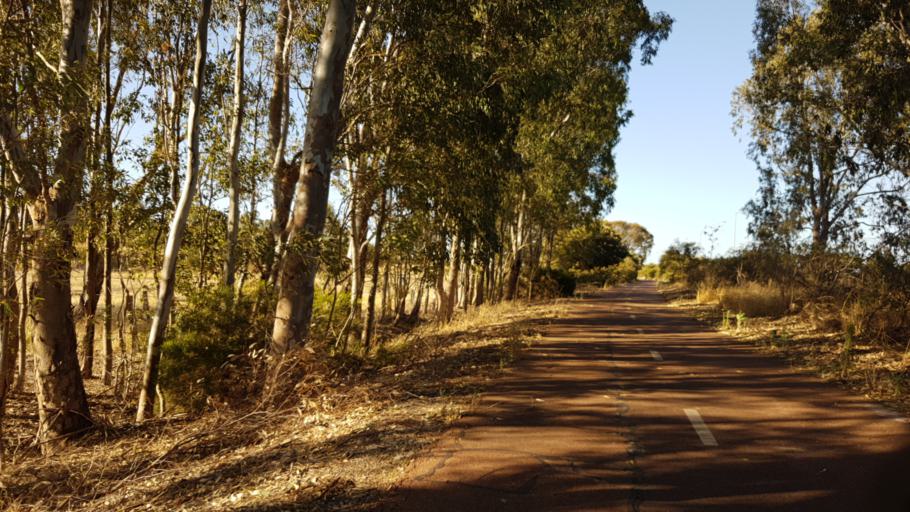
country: AU
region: Western Australia
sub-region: Kwinana
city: Wellard
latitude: -32.2884
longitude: 115.8367
